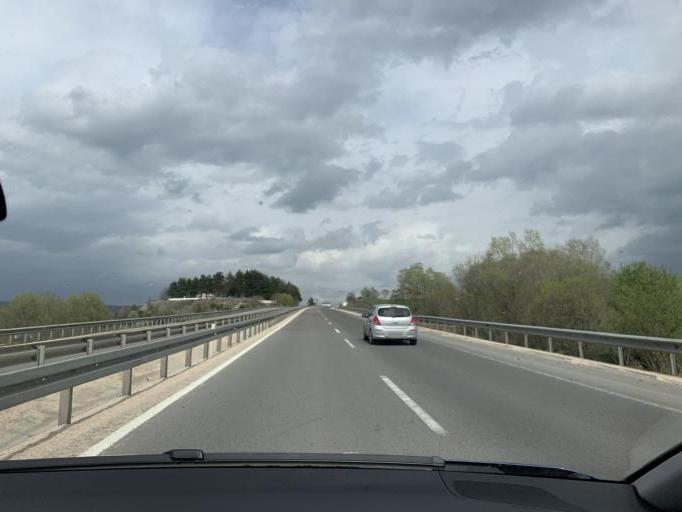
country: TR
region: Bolu
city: Yenicaga
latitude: 40.7820
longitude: 32.0738
